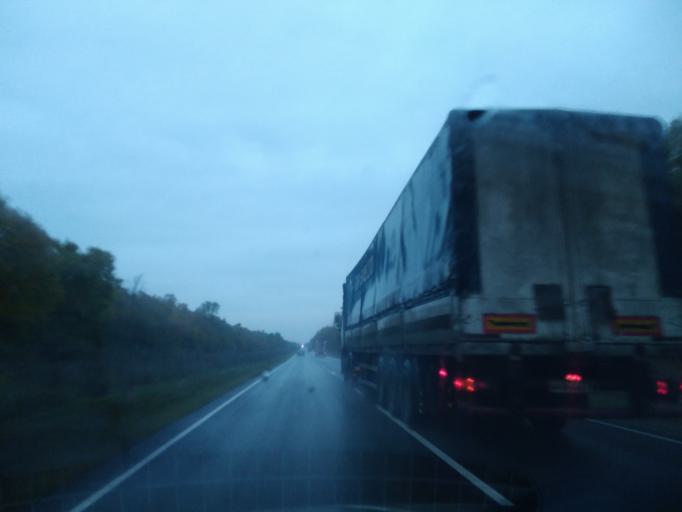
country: RU
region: Tula
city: Teploye
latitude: 53.5220
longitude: 37.6840
